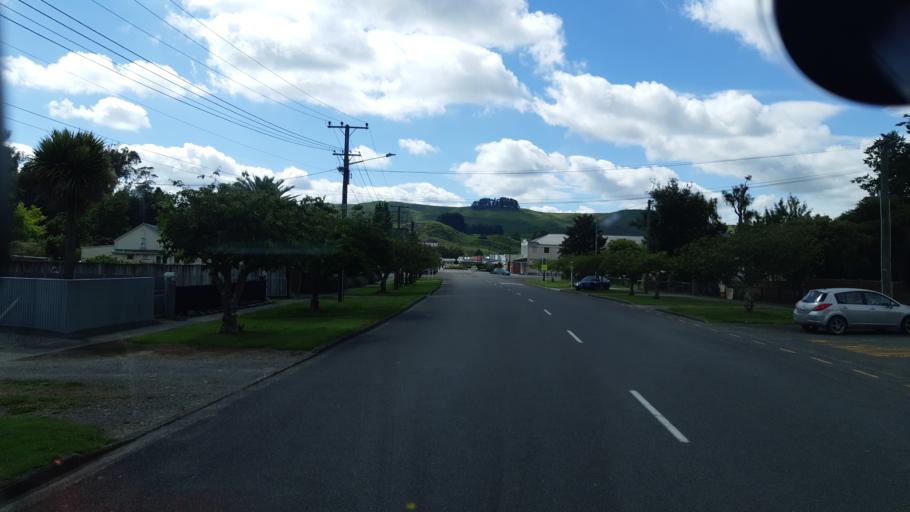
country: NZ
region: Manawatu-Wanganui
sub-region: Rangitikei District
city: Bulls
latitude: -39.9351
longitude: 175.5654
